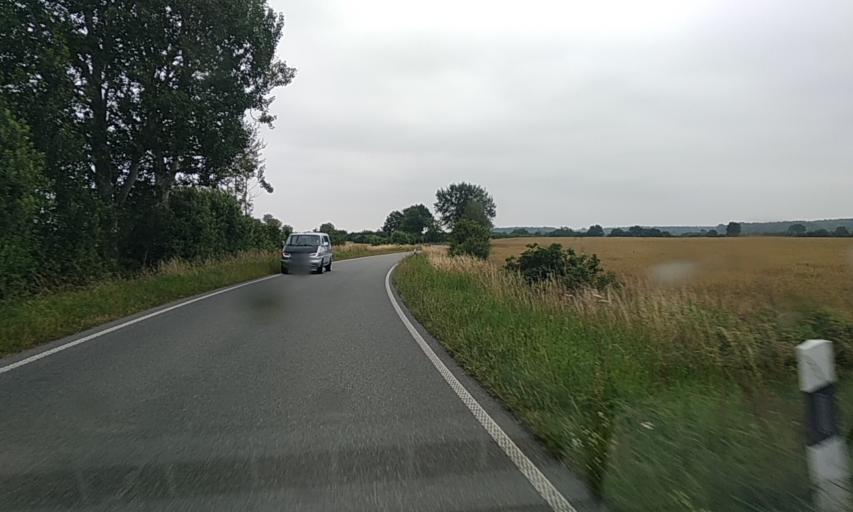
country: DE
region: Schleswig-Holstein
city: Loit
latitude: 54.6074
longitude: 9.7201
